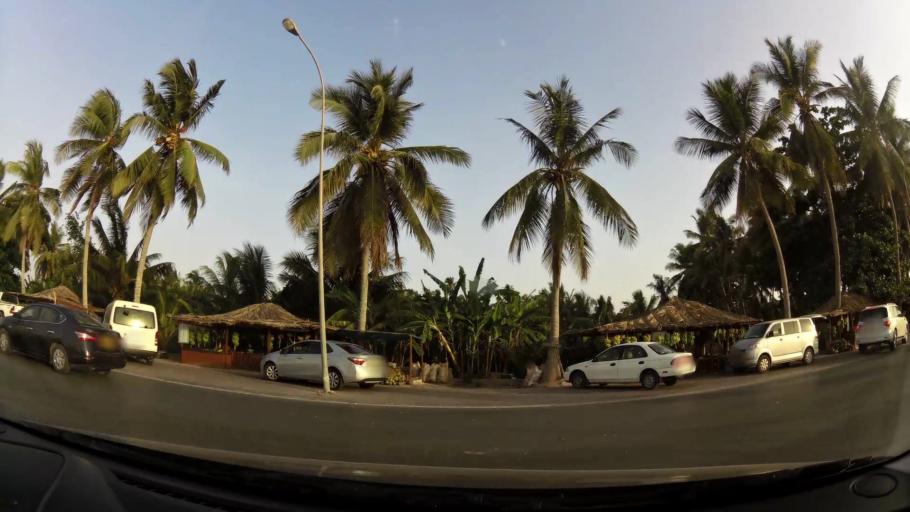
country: OM
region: Zufar
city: Salalah
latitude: 17.0108
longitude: 54.1064
